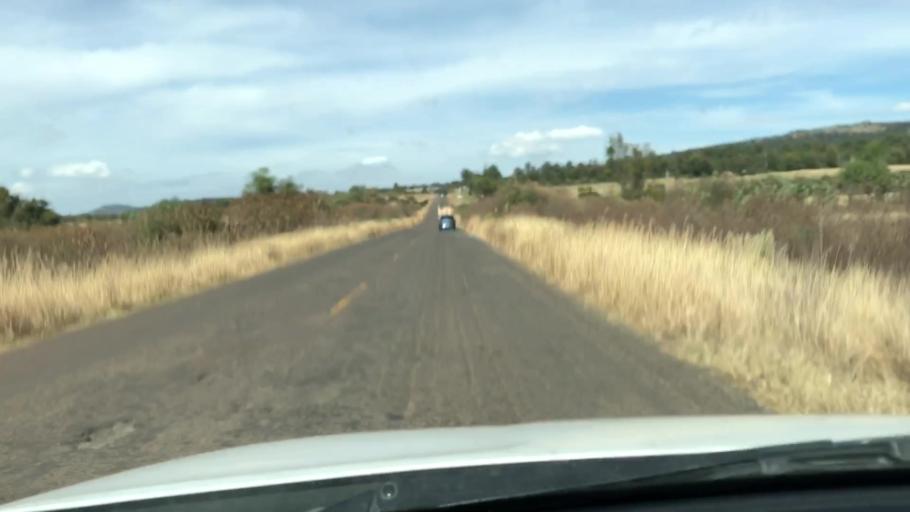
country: MX
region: Jalisco
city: Chiquilistlan
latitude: 20.1649
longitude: -103.7240
